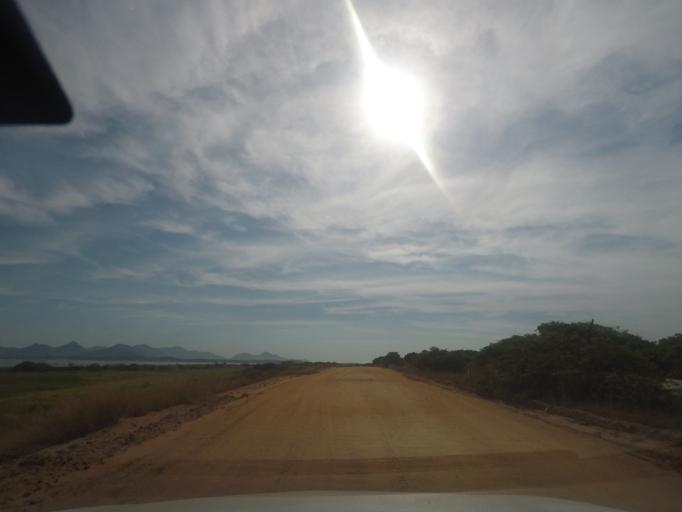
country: BR
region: Rio de Janeiro
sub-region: Marica
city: Marica
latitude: -22.9597
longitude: -42.8706
